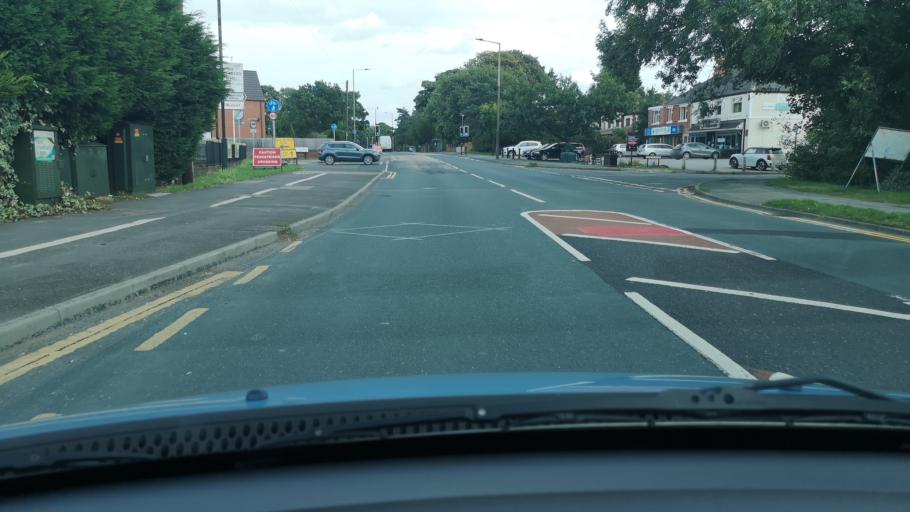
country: GB
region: England
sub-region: Doncaster
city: Kirk Sandall
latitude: 53.5526
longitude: -1.0682
